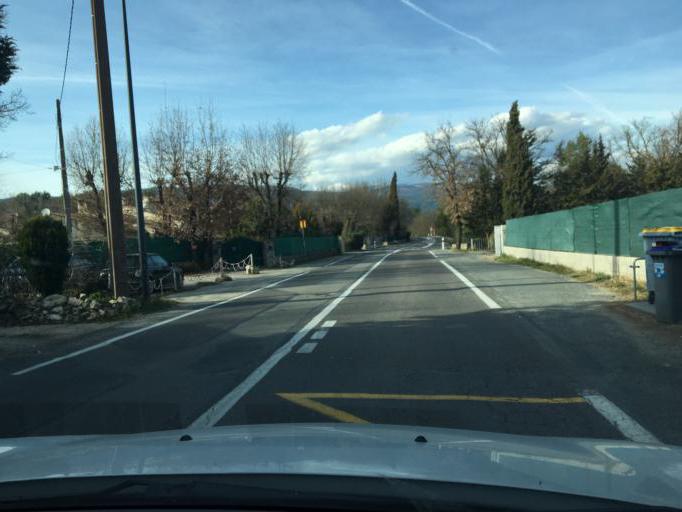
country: FR
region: Provence-Alpes-Cote d'Azur
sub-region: Departement du Var
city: Fayence
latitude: 43.5975
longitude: 6.6902
